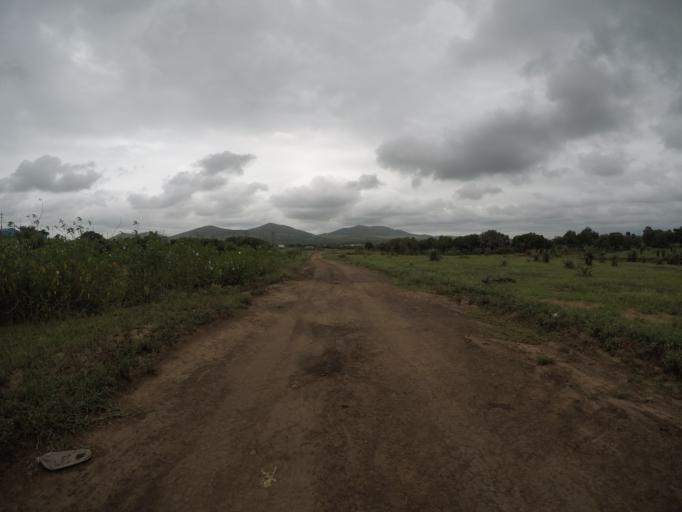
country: ZA
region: KwaZulu-Natal
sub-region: uThungulu District Municipality
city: Empangeni
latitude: -28.6076
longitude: 31.8652
